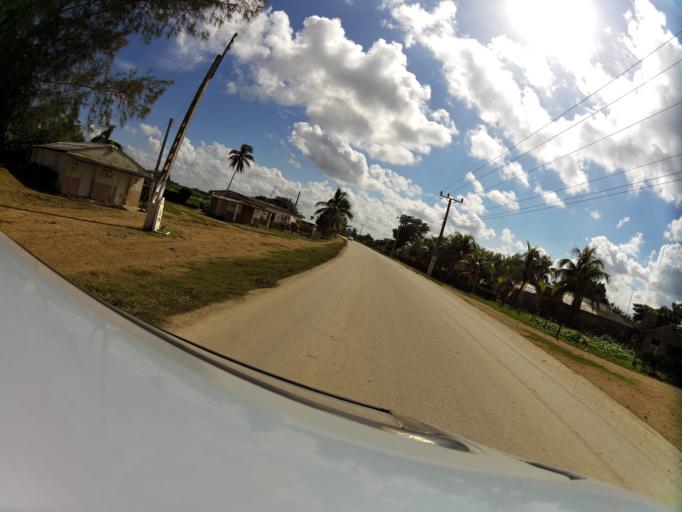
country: CU
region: Las Tunas
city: Jesus Menendez
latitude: 21.2250
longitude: -76.4239
